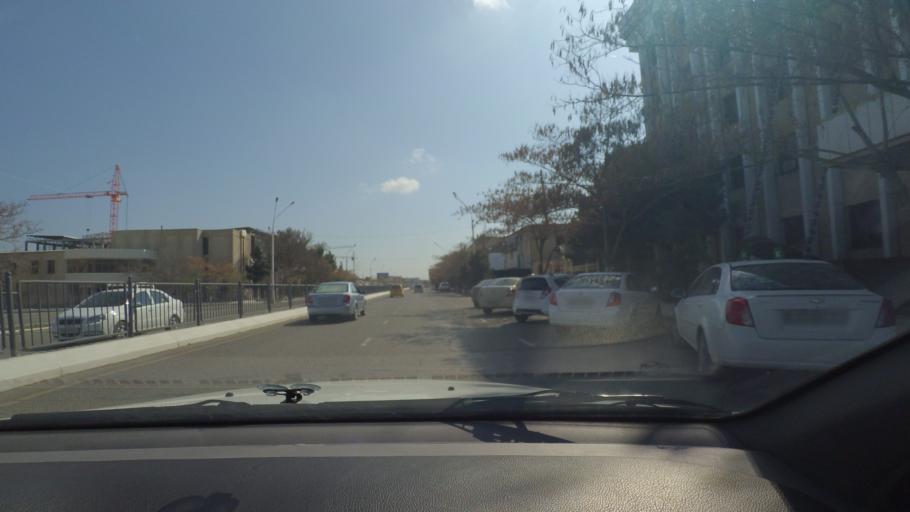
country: UZ
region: Bukhara
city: Bukhara
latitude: 39.7696
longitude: 64.4306
